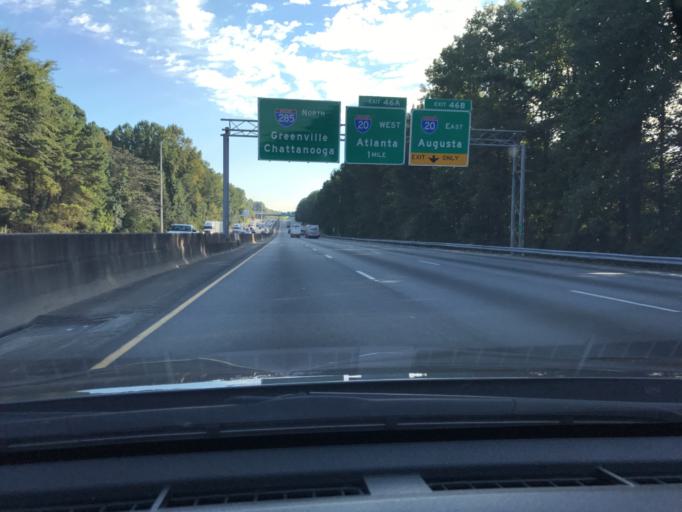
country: US
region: Georgia
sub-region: DeKalb County
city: Panthersville
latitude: 33.7040
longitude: -84.2503
